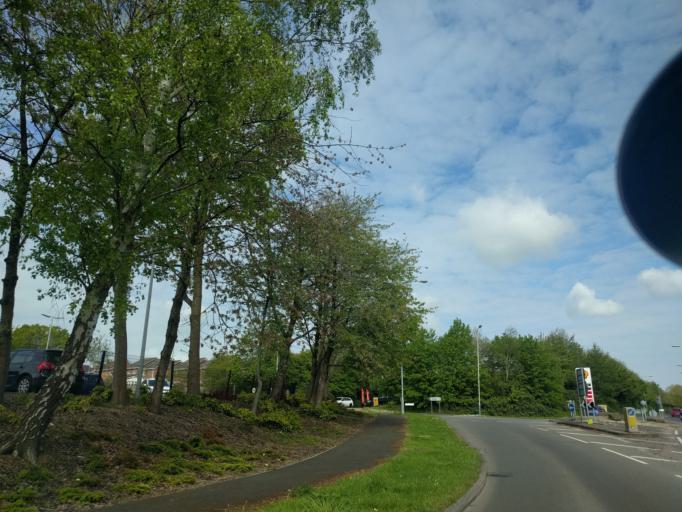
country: GB
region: England
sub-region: Wiltshire
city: Lydiard Tregoze
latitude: 51.5663
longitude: -1.8253
